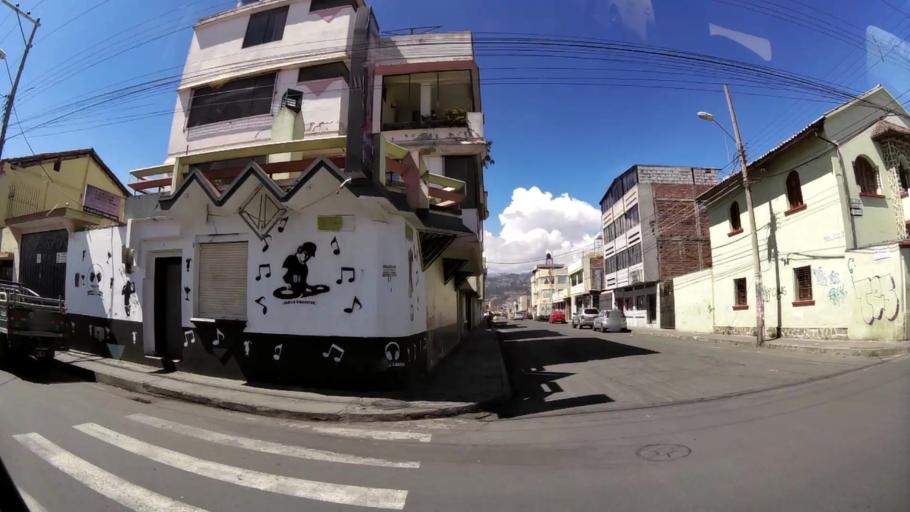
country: EC
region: Chimborazo
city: Riobamba
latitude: -1.6778
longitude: -78.6442
